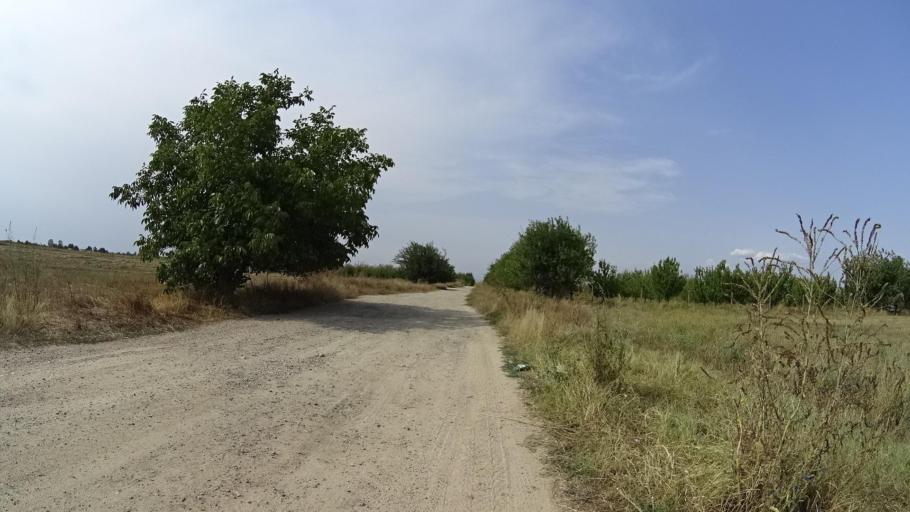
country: BG
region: Plovdiv
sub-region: Obshtina Kaloyanovo
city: Kaloyanovo
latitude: 42.2765
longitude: 24.8001
